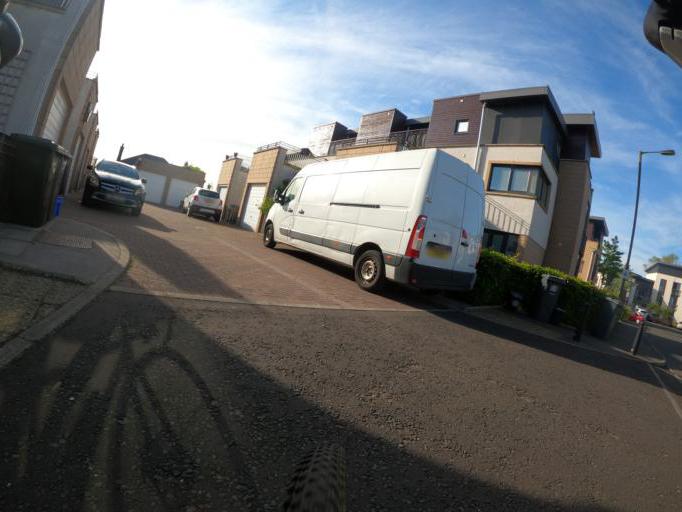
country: GB
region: Scotland
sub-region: Edinburgh
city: Edinburgh
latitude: 55.9737
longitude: -3.2245
